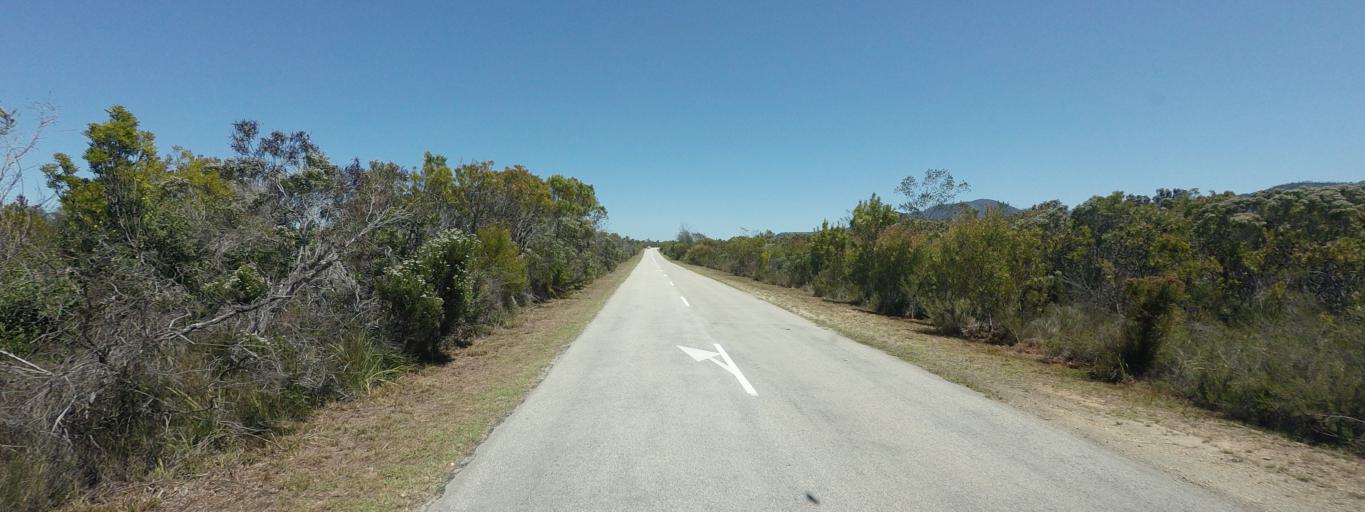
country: ZA
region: Western Cape
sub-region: Eden District Municipality
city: Plettenberg Bay
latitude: -33.9586
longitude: 23.5207
